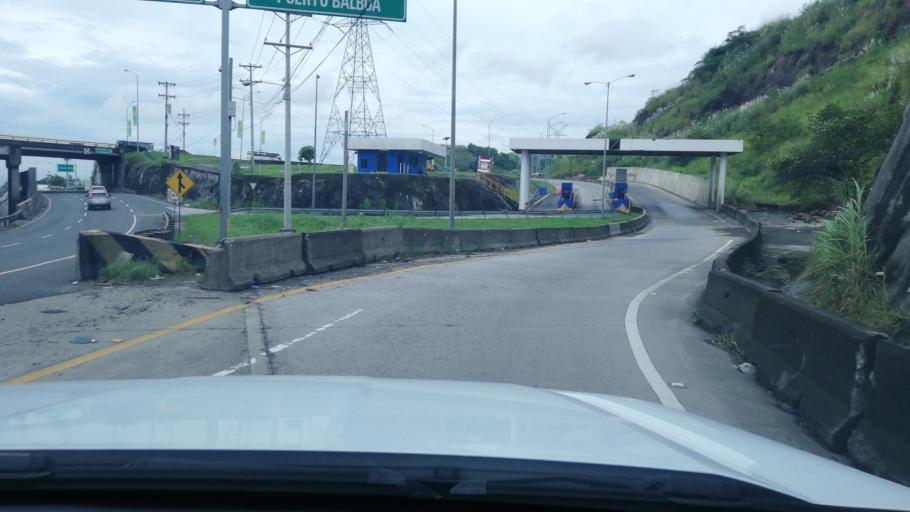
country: PA
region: Panama
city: Las Cumbres
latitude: 9.0604
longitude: -79.5102
